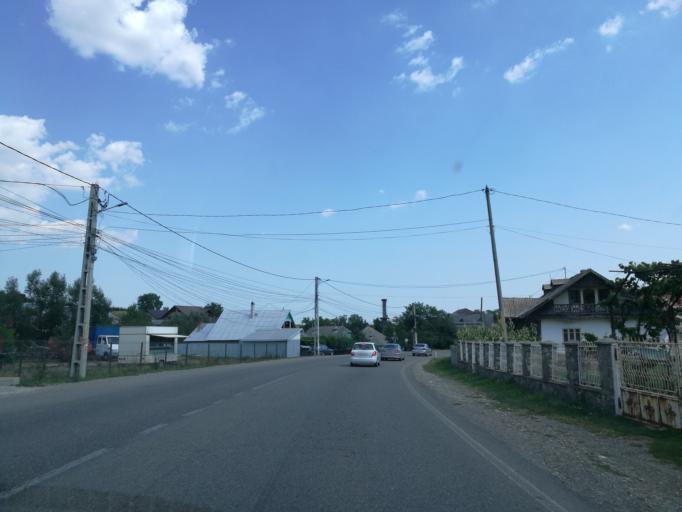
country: RO
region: Neamt
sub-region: Comuna Baltatesti
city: Baltatesti
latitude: 47.1254
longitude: 26.3108
